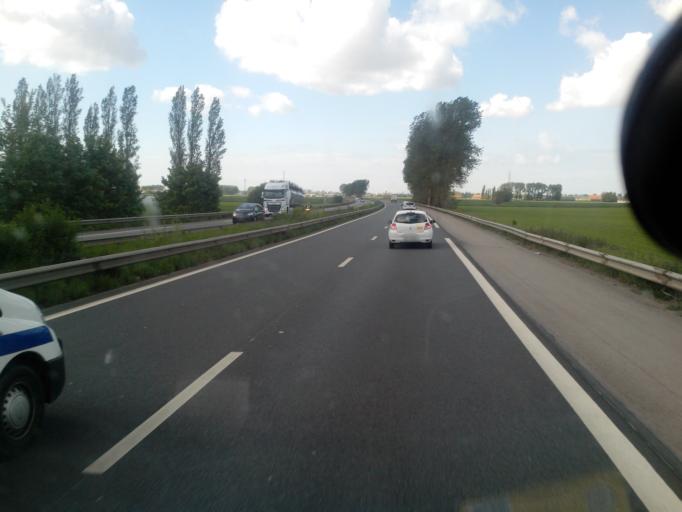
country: FR
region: Nord-Pas-de-Calais
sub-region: Departement du Nord
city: Bierne
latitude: 50.9733
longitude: 2.3928
